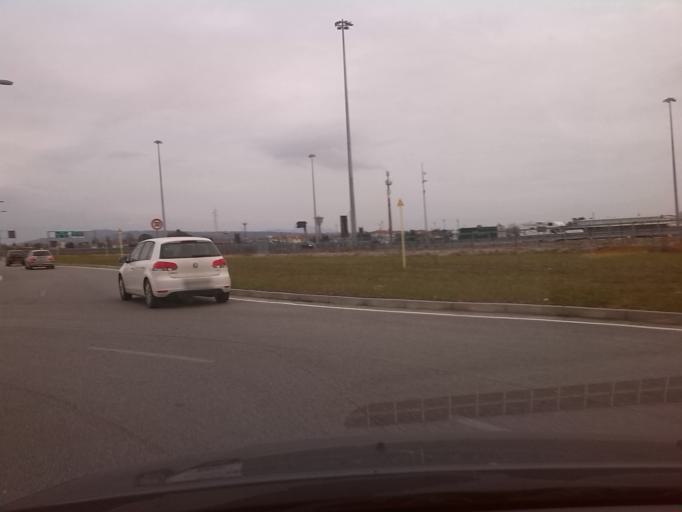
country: IT
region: Friuli Venezia Giulia
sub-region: Provincia di Gorizia
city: Villesse
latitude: 45.8640
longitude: 13.4314
